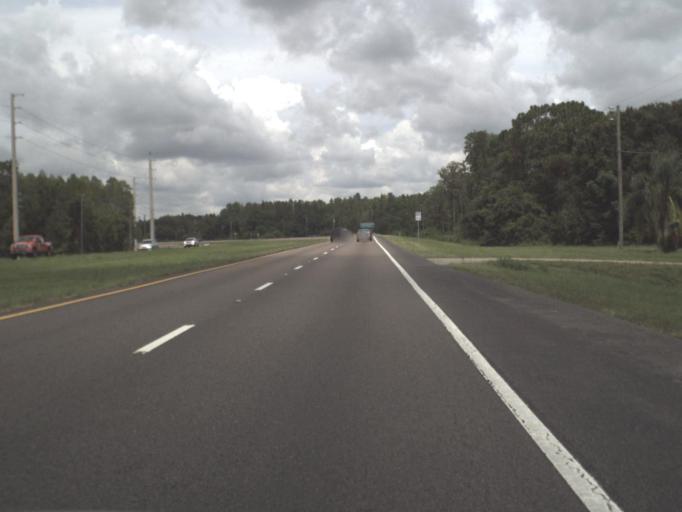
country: US
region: Florida
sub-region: Pasco County
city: Land O' Lakes
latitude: 28.1964
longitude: -82.4855
